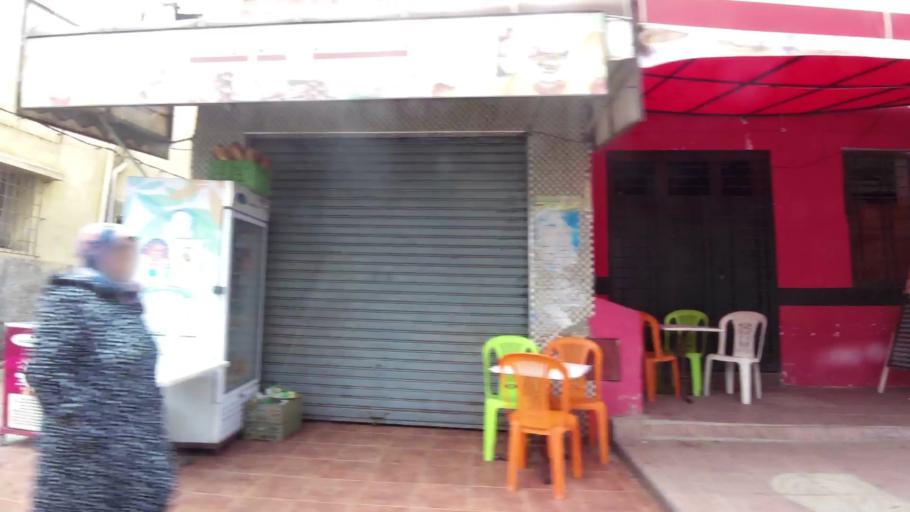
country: MA
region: Doukkala-Abda
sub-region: El-Jadida
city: El Jadida
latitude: 33.2468
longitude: -8.4977
